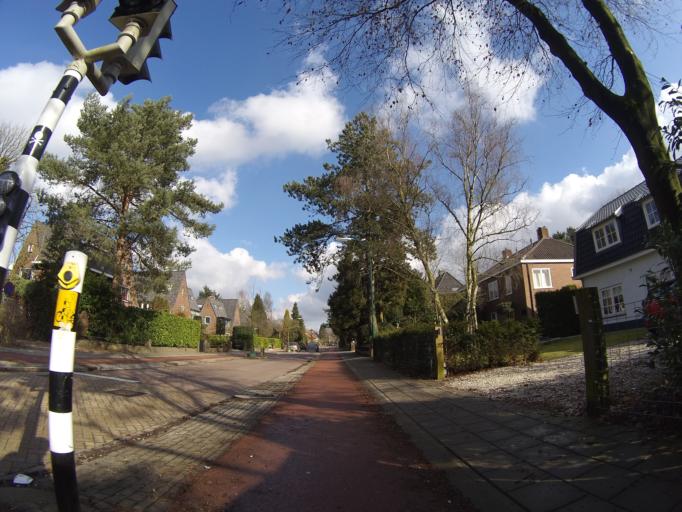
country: NL
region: Utrecht
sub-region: Gemeente Zeist
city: Zeist
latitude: 52.1339
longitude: 5.2208
